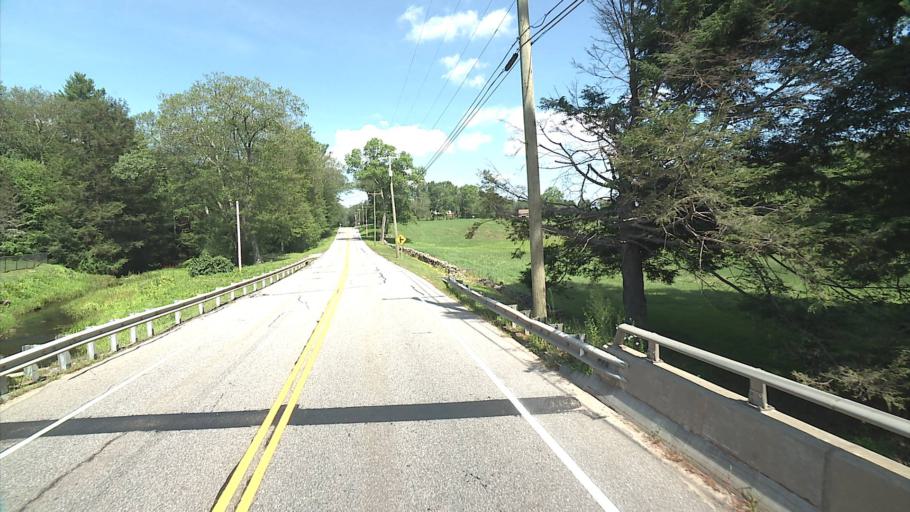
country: US
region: Connecticut
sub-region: Windham County
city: South Woodstock
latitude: 41.9176
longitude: -72.0781
